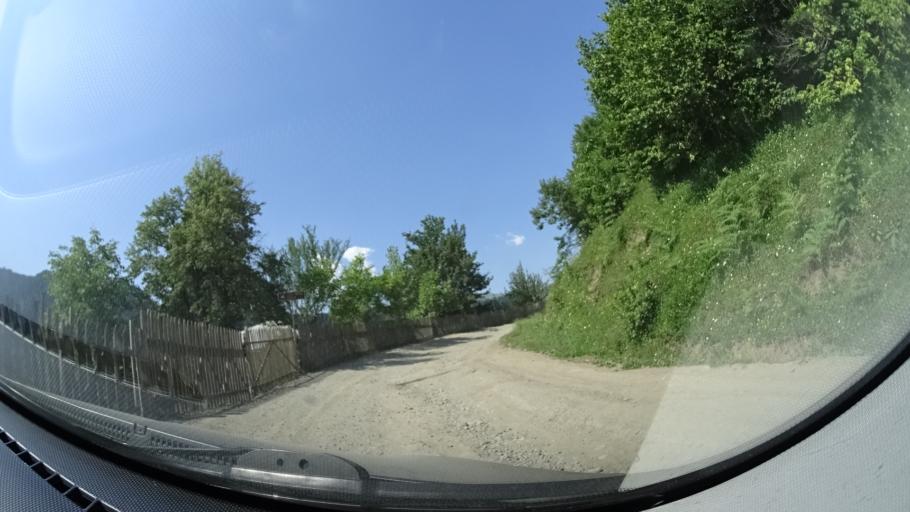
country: GE
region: Ajaria
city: Dioknisi
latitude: 41.6490
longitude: 42.4587
